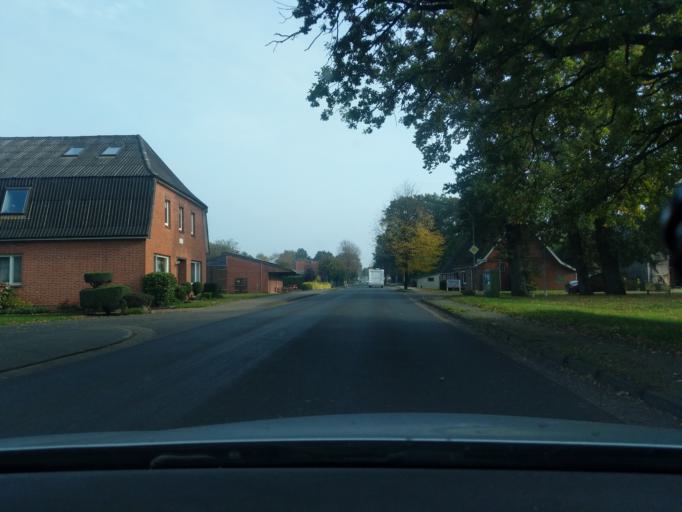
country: DE
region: Lower Saxony
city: Mittelstenahe
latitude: 53.6510
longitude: 9.0394
